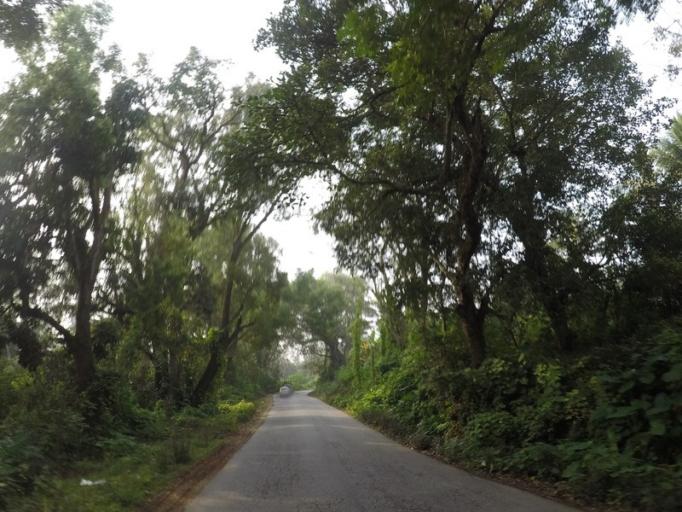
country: IN
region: Karnataka
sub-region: Chikmagalur
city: Chikmagalur
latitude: 13.2645
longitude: 75.6871
